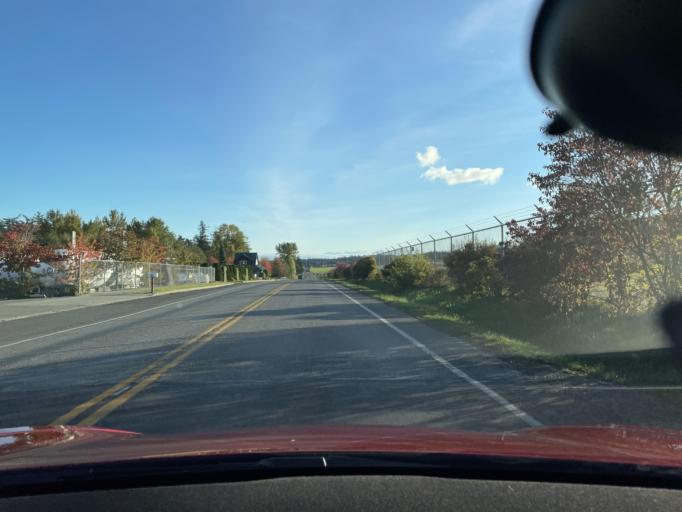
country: US
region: Washington
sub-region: San Juan County
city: Friday Harbor
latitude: 48.5279
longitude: -123.0232
